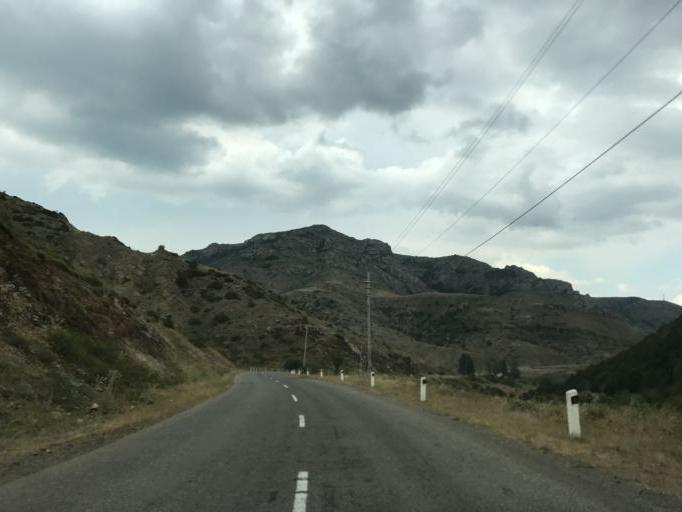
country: AZ
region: Susa
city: Shushi
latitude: 39.7147
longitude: 46.6633
